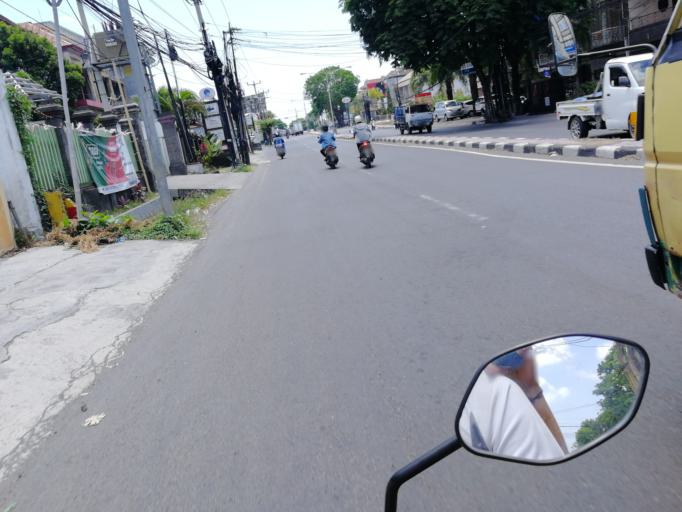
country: ID
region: Bali
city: Banjar Kertasari
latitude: -8.6368
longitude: 115.1830
